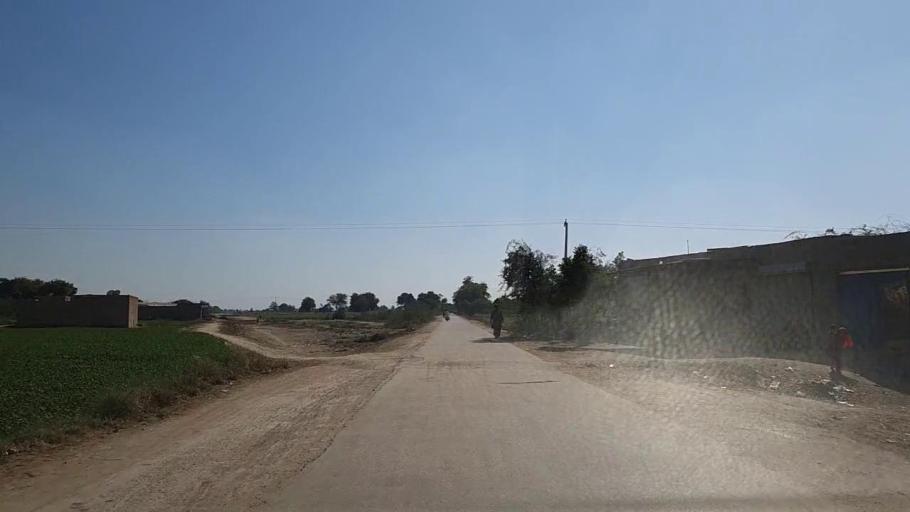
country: PK
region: Sindh
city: Nawabshah
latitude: 26.2437
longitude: 68.4457
